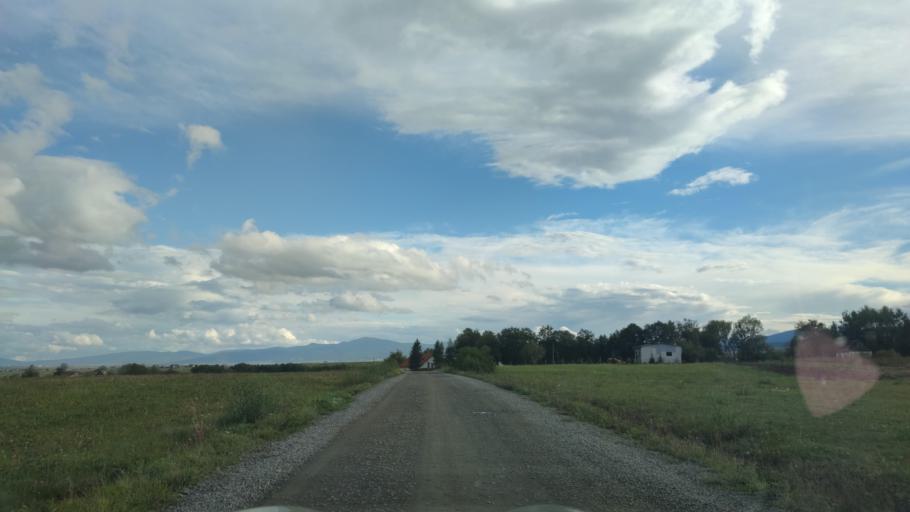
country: RO
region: Harghita
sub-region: Comuna Remetea
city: Remetea
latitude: 46.8154
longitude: 25.4220
